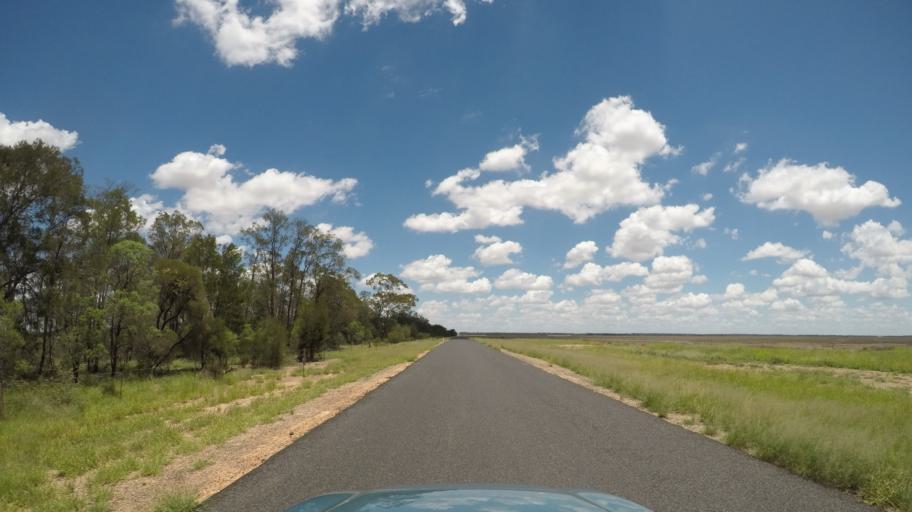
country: AU
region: Queensland
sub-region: Goondiwindi
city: Goondiwindi
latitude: -28.1723
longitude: 150.2291
